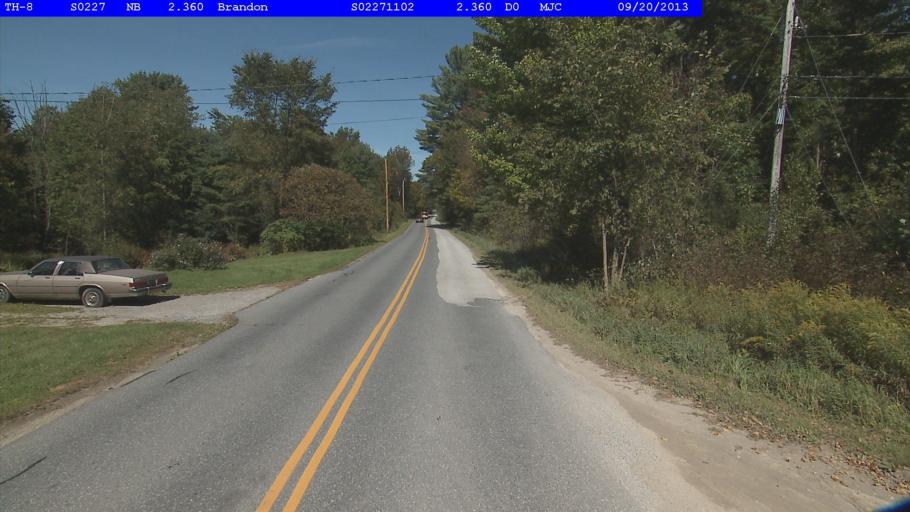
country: US
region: Vermont
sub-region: Rutland County
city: Brandon
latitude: 43.8084
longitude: -73.0565
